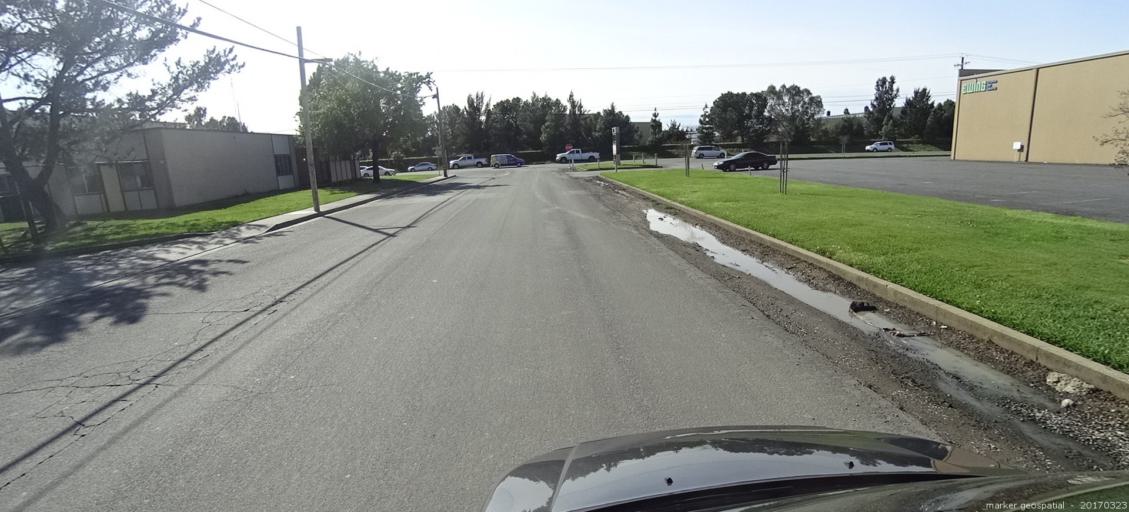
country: US
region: California
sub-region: Sacramento County
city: Florin
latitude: 38.5215
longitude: -121.3897
